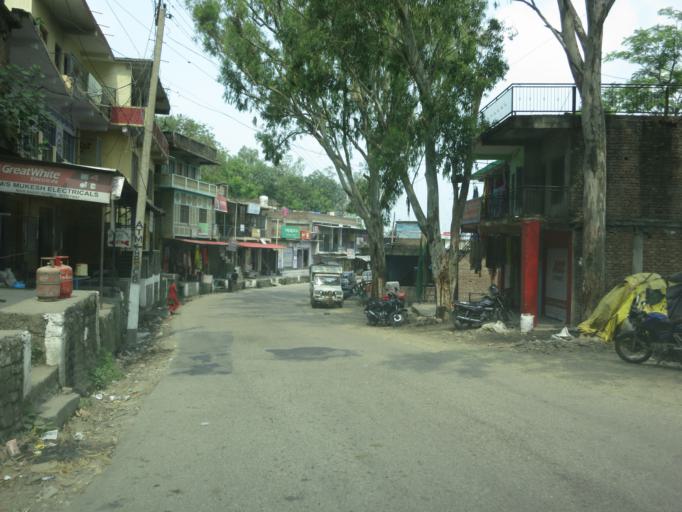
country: IN
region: Himachal Pradesh
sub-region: Bilaspur
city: Bilaspur
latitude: 31.2551
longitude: 76.8609
